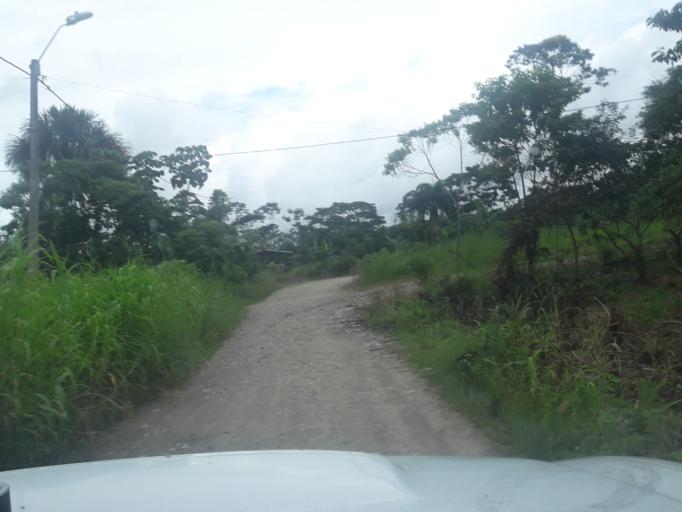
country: EC
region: Napo
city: Archidona
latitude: -0.9514
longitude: -77.8112
